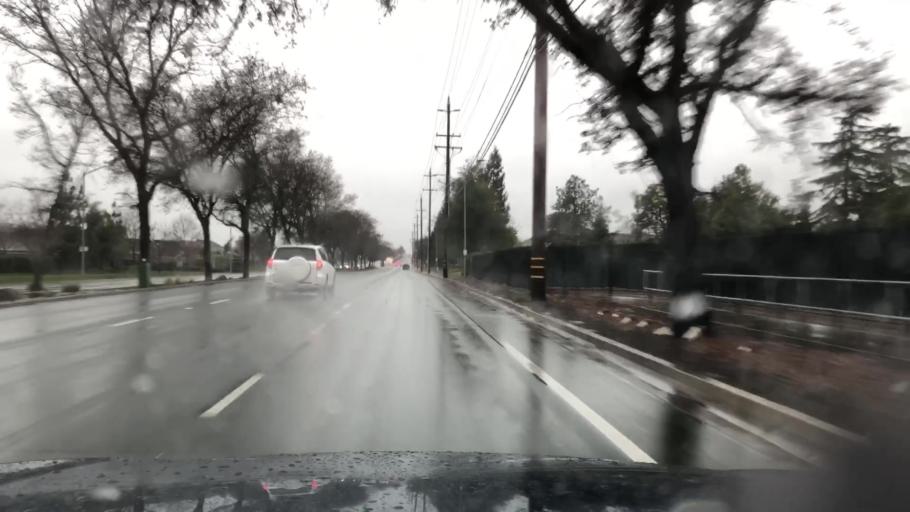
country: US
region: California
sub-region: Sacramento County
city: Laguna
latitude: 38.4088
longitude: -121.4431
